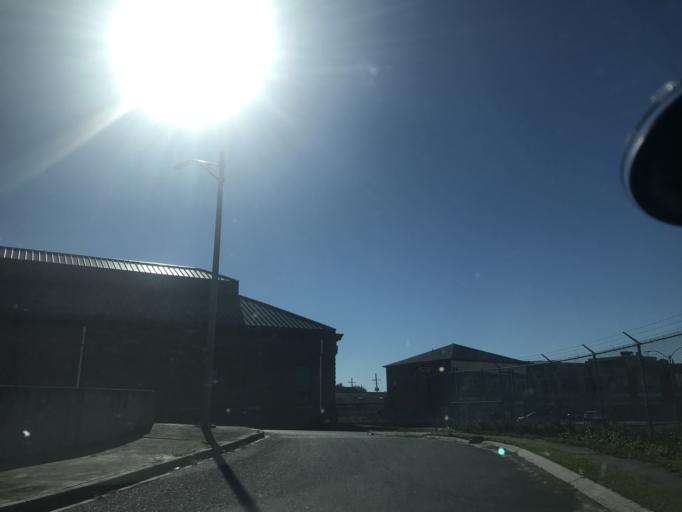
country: US
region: Louisiana
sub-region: Orleans Parish
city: New Orleans
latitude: 29.9521
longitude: -90.0993
